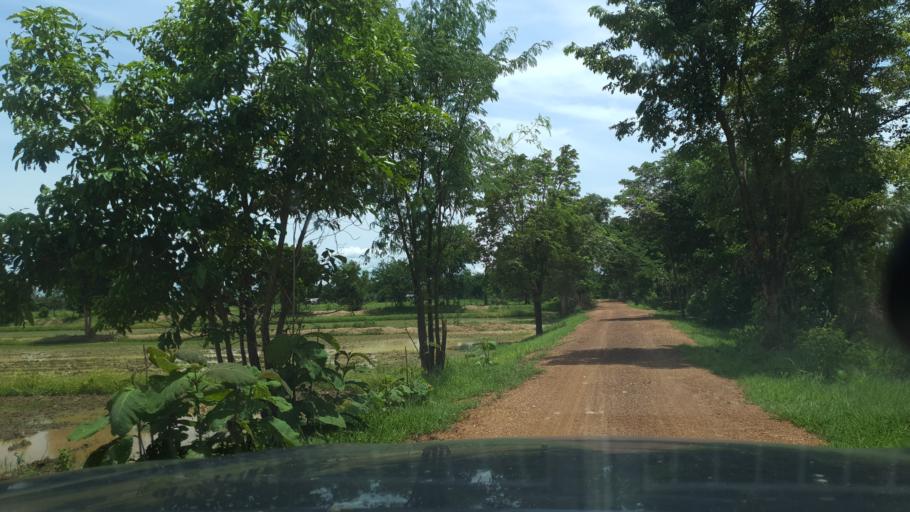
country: TH
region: Sukhothai
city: Ban Na
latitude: 17.0706
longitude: 99.6971
